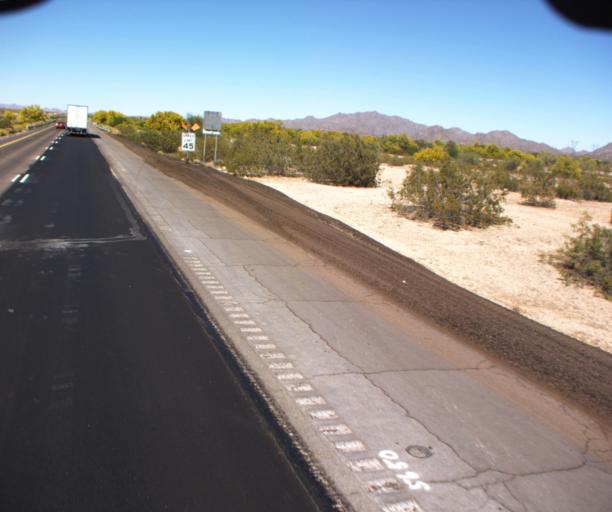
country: US
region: Arizona
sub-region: Maricopa County
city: Gila Bend
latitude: 33.0716
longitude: -112.6459
